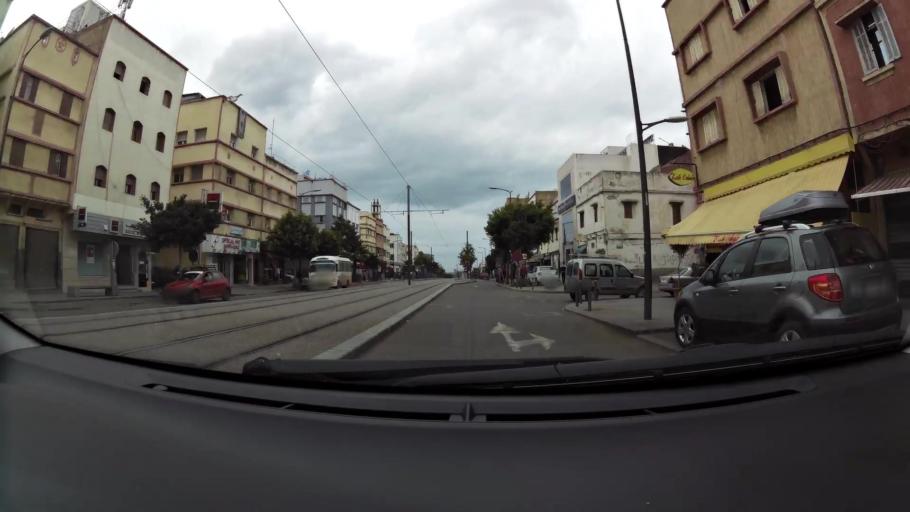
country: MA
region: Grand Casablanca
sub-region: Casablanca
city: Casablanca
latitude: 33.5880
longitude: -7.5675
